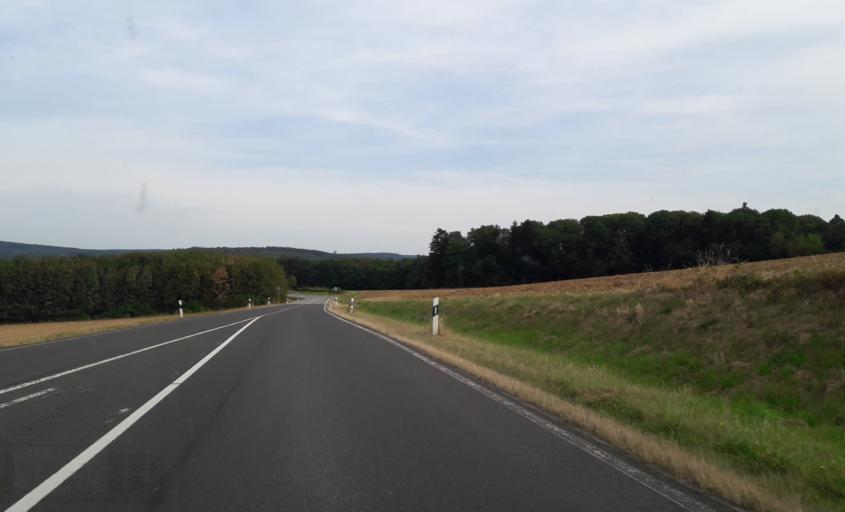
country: DE
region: Rheinland-Pfalz
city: Rinzenberg
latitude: 49.6706
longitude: 7.1461
